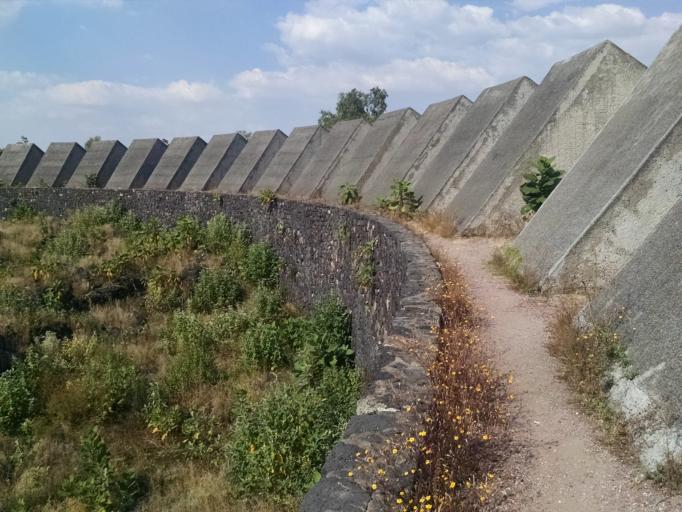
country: MX
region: Mexico City
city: Tlalpan
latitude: 19.3184
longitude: -99.1816
